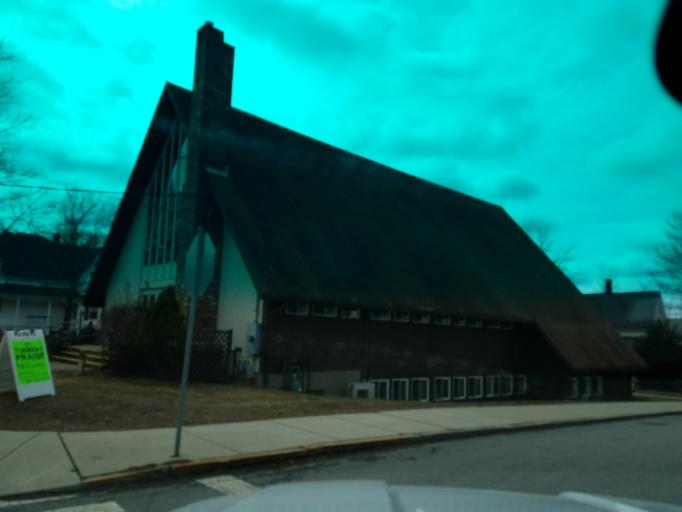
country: US
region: Connecticut
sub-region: Windham County
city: Danielson
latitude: 41.8063
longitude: -71.8800
